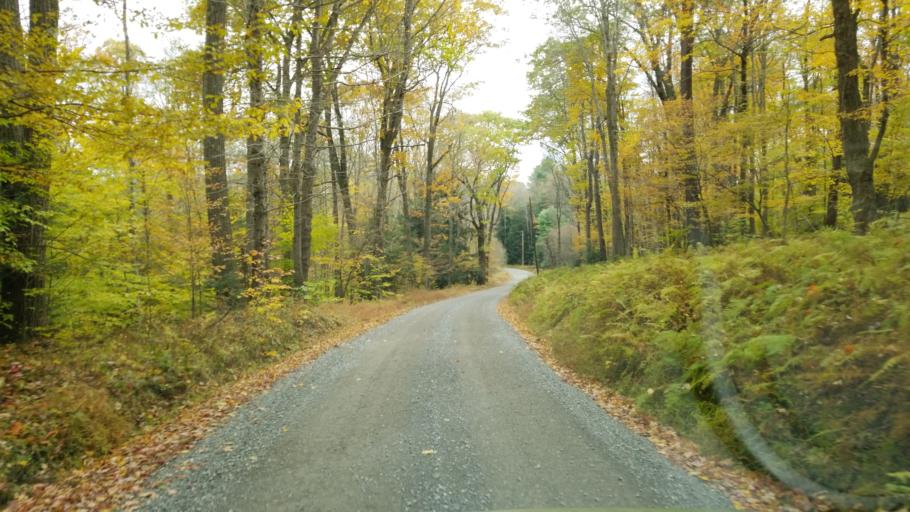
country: US
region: Pennsylvania
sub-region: Clearfield County
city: Clearfield
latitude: 41.1971
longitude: -78.4098
